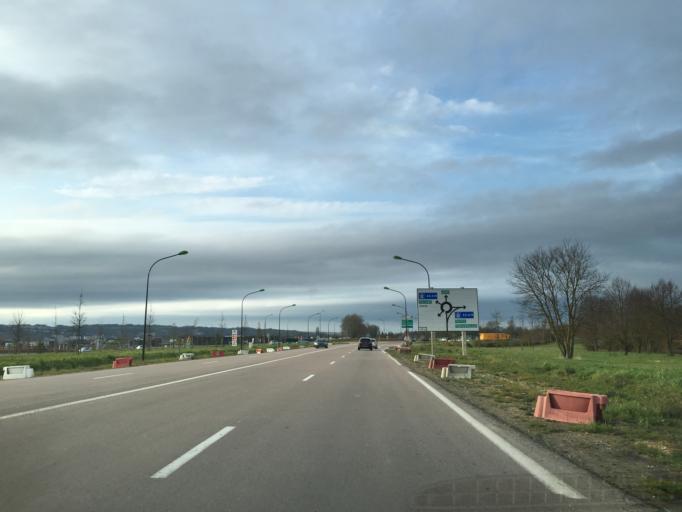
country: FR
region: Bourgogne
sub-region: Departement de l'Yonne
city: Maillot
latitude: 48.1723
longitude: 3.2951
